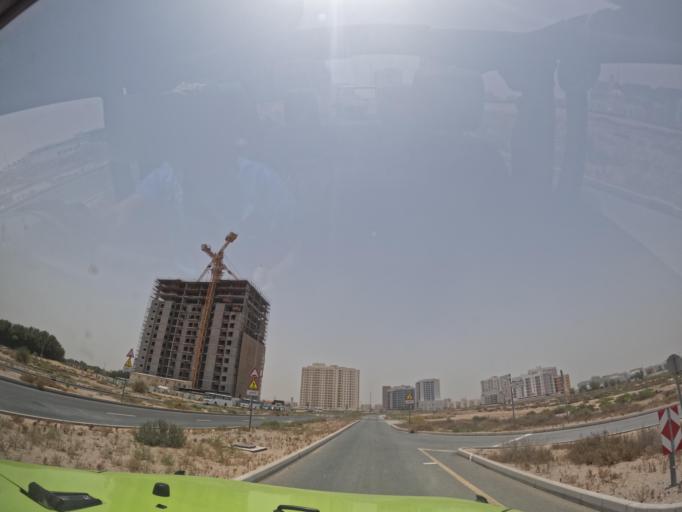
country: AE
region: Dubai
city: Dubai
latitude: 25.0922
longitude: 55.3759
